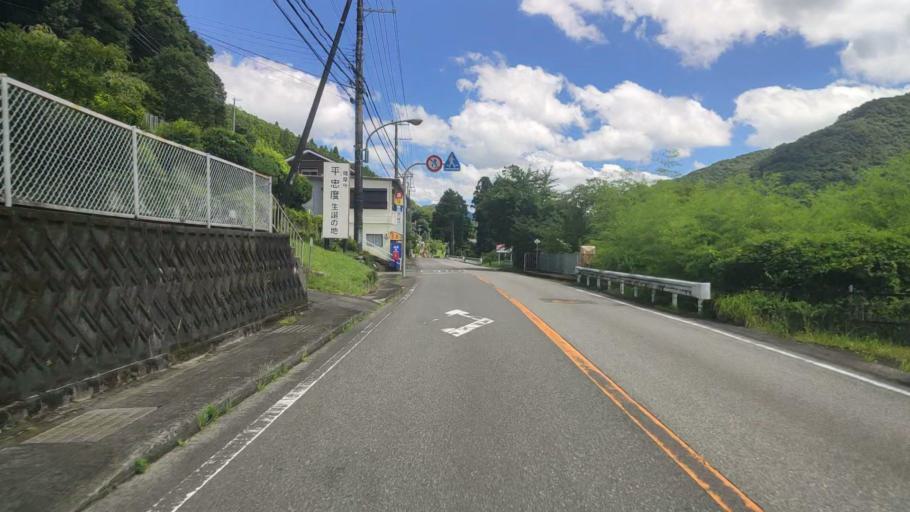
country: JP
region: Wakayama
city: Shingu
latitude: 33.8256
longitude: 135.8559
